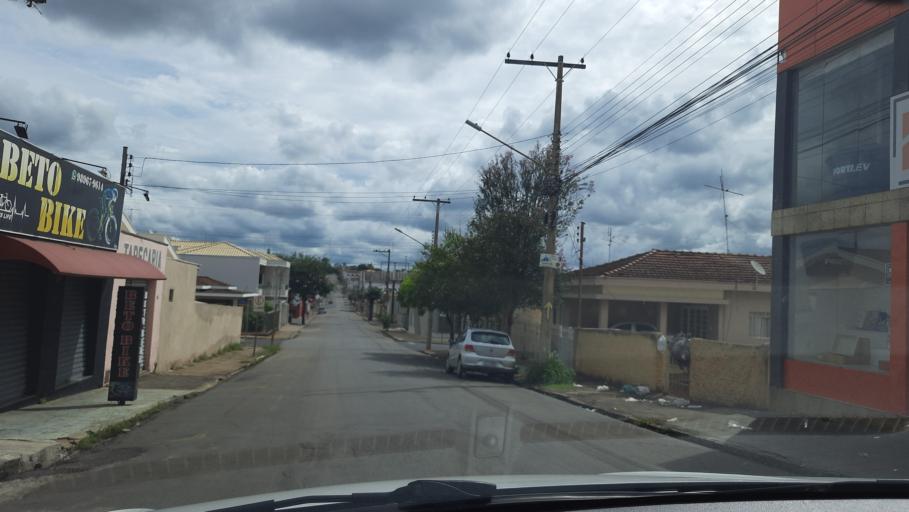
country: BR
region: Sao Paulo
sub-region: Vargem Grande Do Sul
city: Vargem Grande do Sul
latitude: -21.8331
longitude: -46.8955
